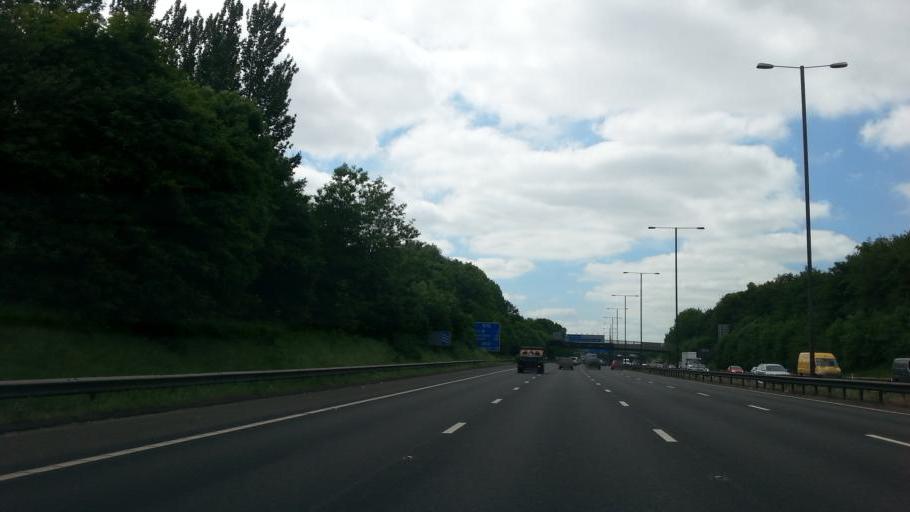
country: GB
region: England
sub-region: Manchester
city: Ringway
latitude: 53.3889
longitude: -2.2740
